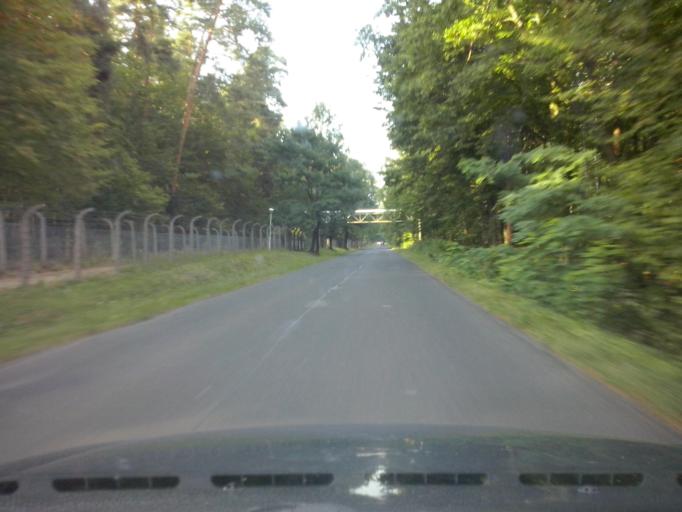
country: PL
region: Subcarpathian Voivodeship
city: Nowa Sarzyna
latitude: 50.3192
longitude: 22.3315
